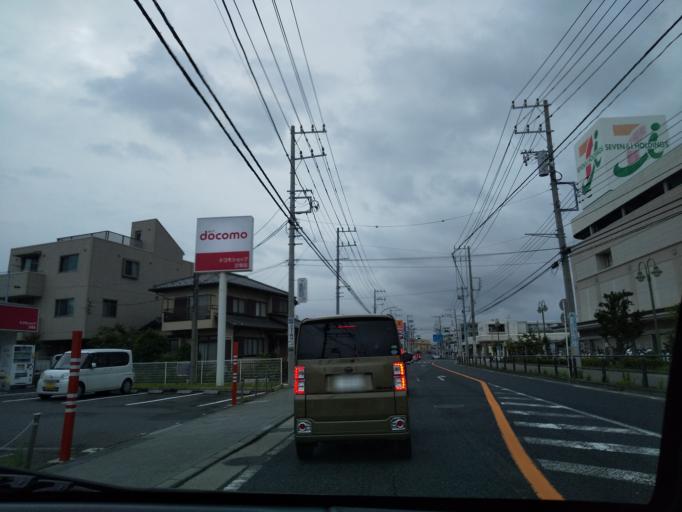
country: JP
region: Kanagawa
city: Fujisawa
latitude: 35.4129
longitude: 139.4997
